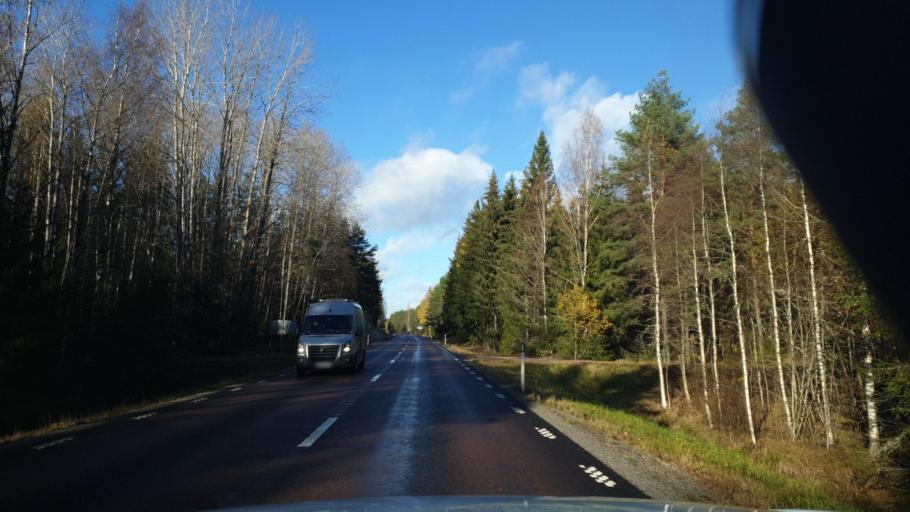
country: SE
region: Vaermland
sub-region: Arvika Kommun
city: Arvika
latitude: 59.5327
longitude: 12.7628
